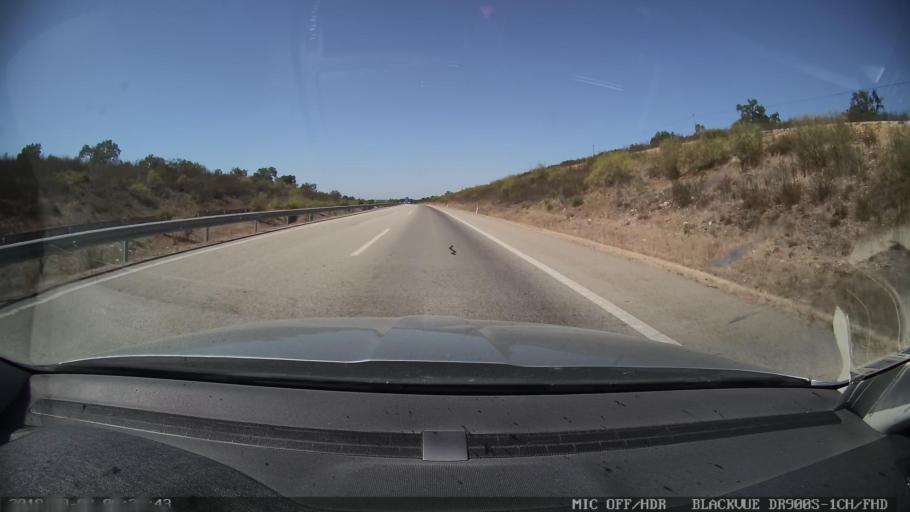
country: PT
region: Evora
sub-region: Vendas Novas
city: Vendas Novas
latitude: 38.6473
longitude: -8.4110
